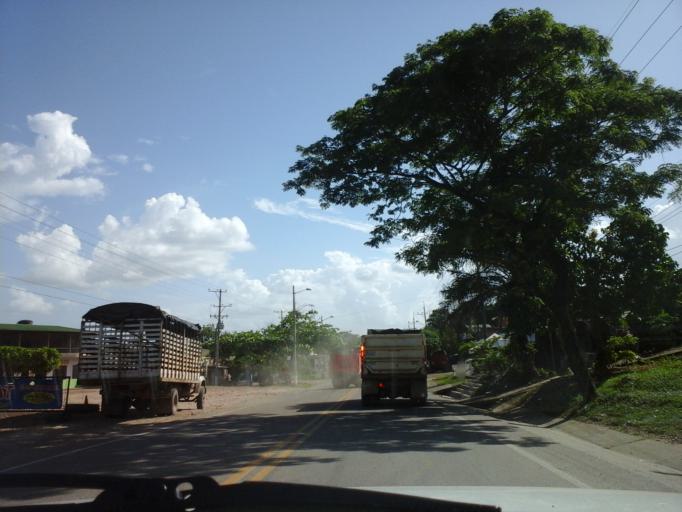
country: CO
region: Meta
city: Puerto Lopez
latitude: 4.0834
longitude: -72.9655
